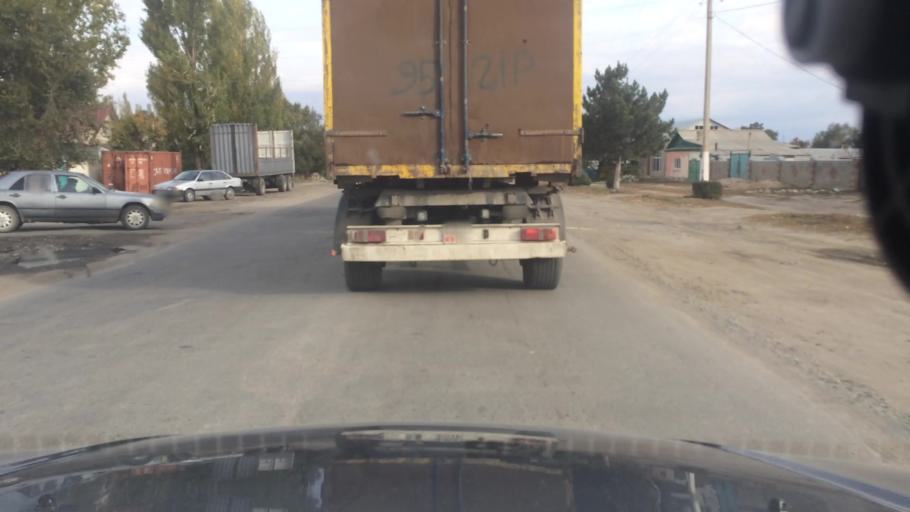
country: KG
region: Ysyk-Koel
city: Karakol
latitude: 42.5181
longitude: 78.3858
